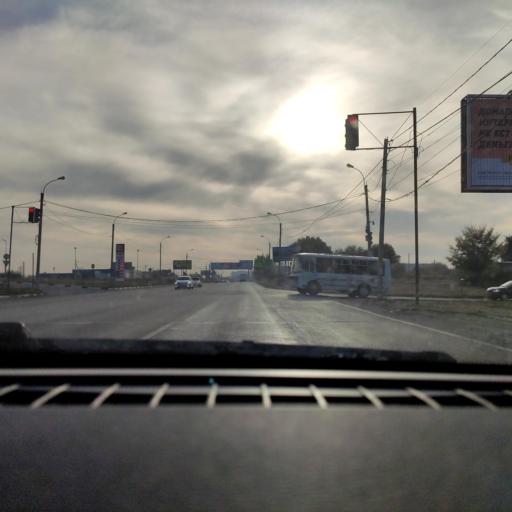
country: RU
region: Voronezj
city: Voronezh
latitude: 51.6806
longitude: 39.2846
